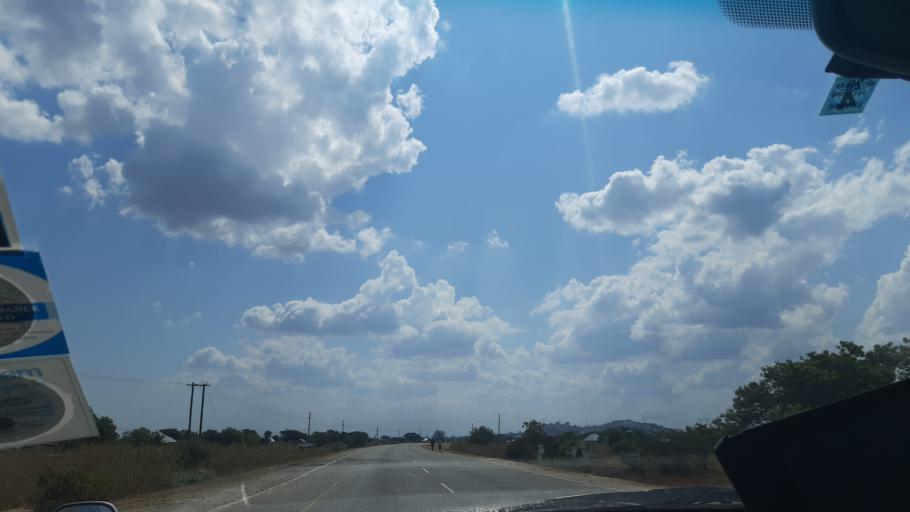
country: TZ
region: Singida
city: Kintinku
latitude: -5.9645
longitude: 35.3287
